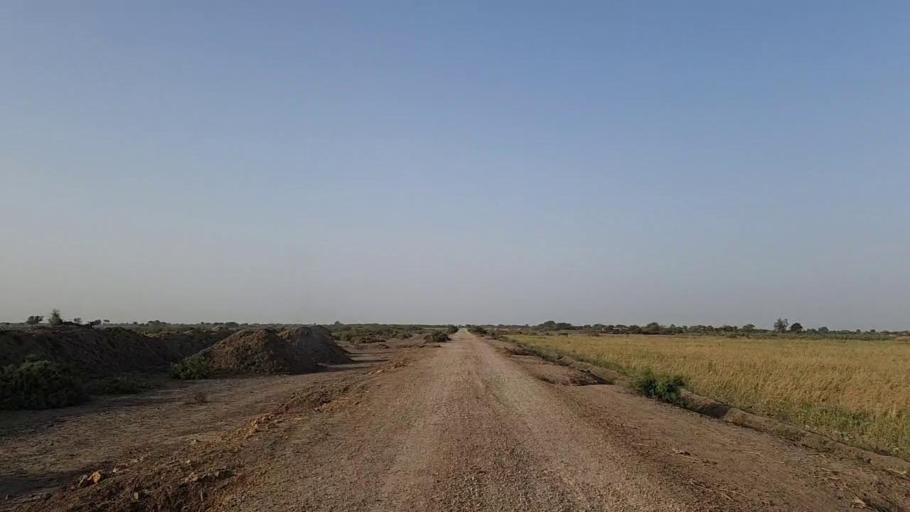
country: PK
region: Sindh
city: Jati
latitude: 24.3738
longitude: 68.1476
